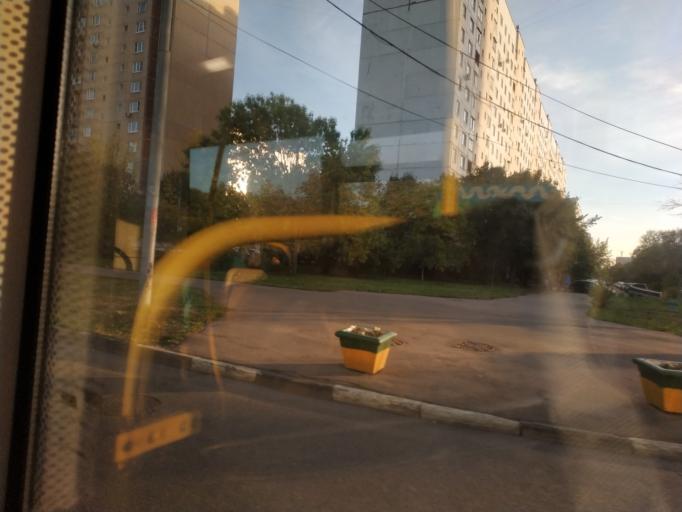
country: RU
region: Moscow
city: Novo-Peredelkino
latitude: 55.6451
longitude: 37.3519
